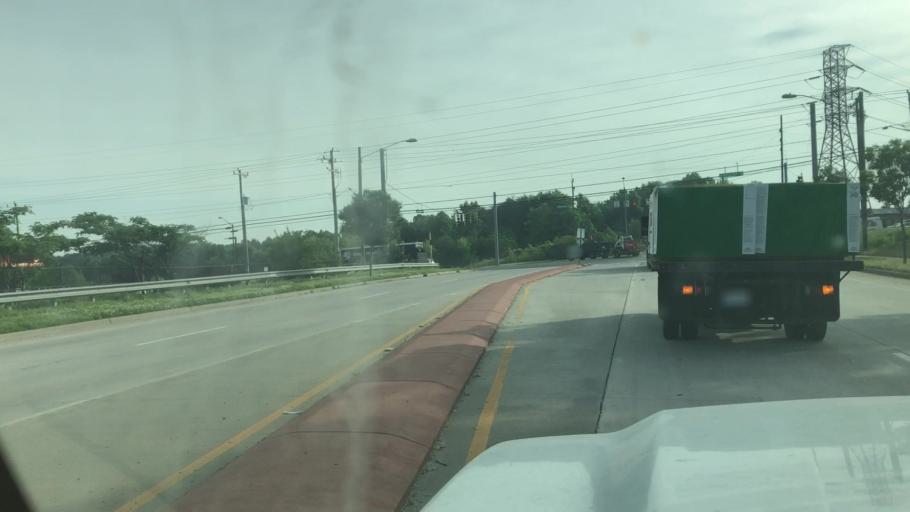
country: US
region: North Carolina
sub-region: Mecklenburg County
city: Charlotte
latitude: 35.2899
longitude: -80.9134
